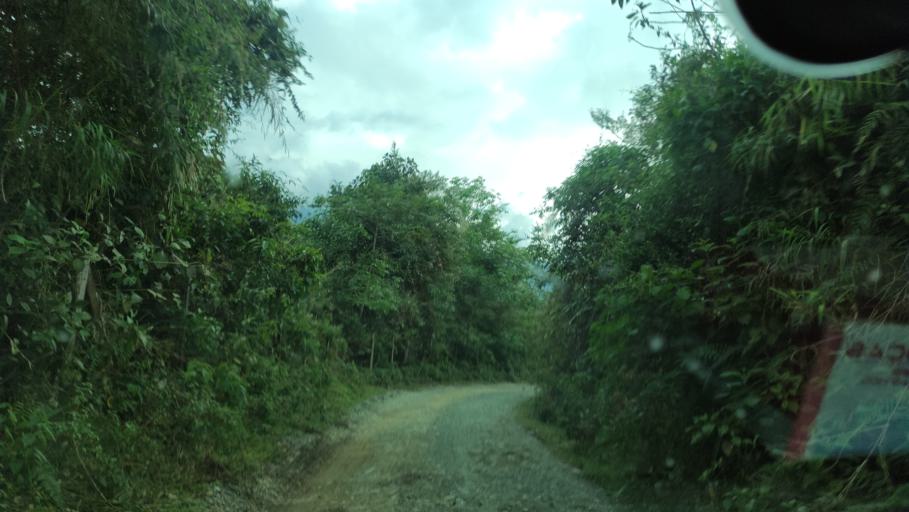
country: CO
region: Valle del Cauca
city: San Pedro
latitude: 3.8772
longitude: -76.1488
